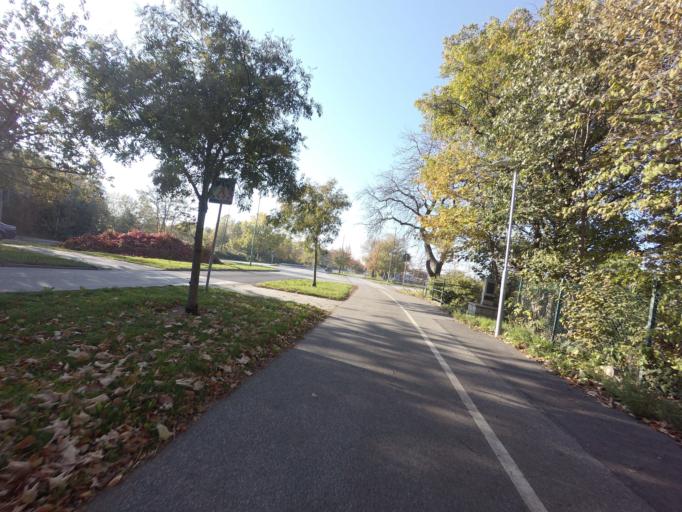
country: SE
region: Skane
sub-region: Burlovs Kommun
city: Arloev
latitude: 55.6290
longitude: 13.0673
